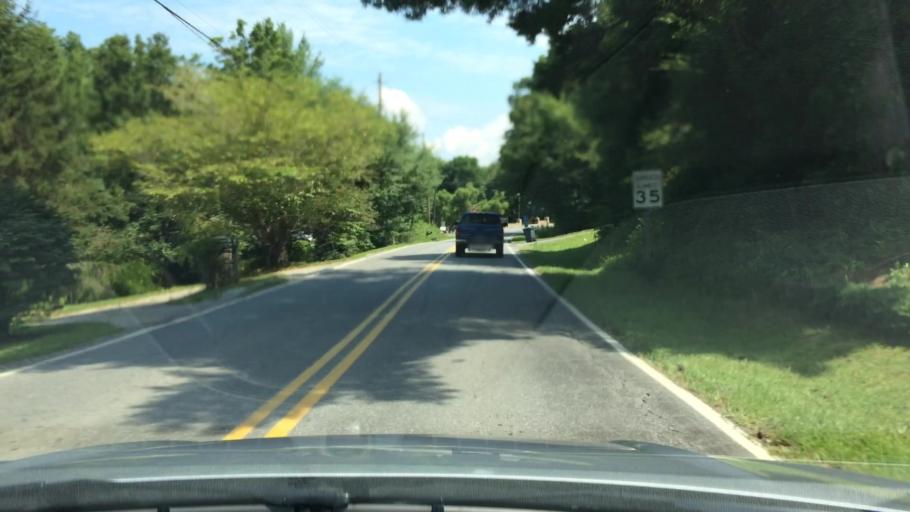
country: US
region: North Carolina
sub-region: Buncombe County
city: Weaverville
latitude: 35.6790
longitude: -82.5904
